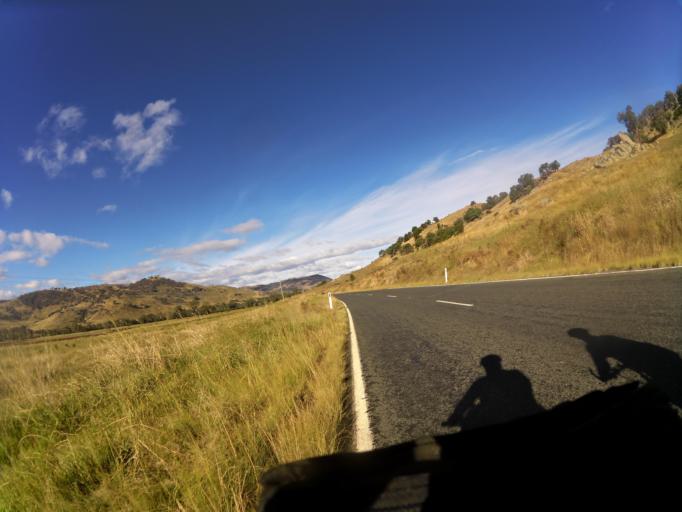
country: AU
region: New South Wales
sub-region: Greater Hume Shire
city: Holbrook
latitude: -35.9656
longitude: 147.7564
